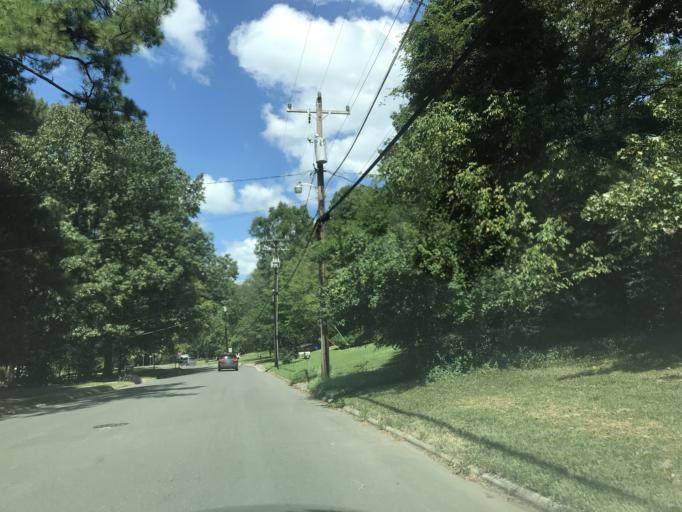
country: US
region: North Carolina
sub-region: Orange County
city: Chapel Hill
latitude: 35.9289
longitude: -79.0193
